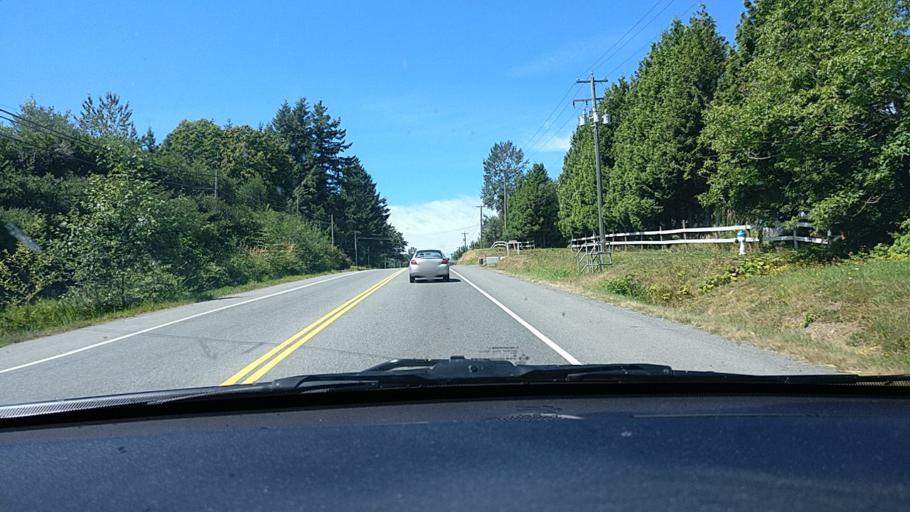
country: CA
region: British Columbia
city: Aldergrove
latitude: 49.0576
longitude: -122.4070
